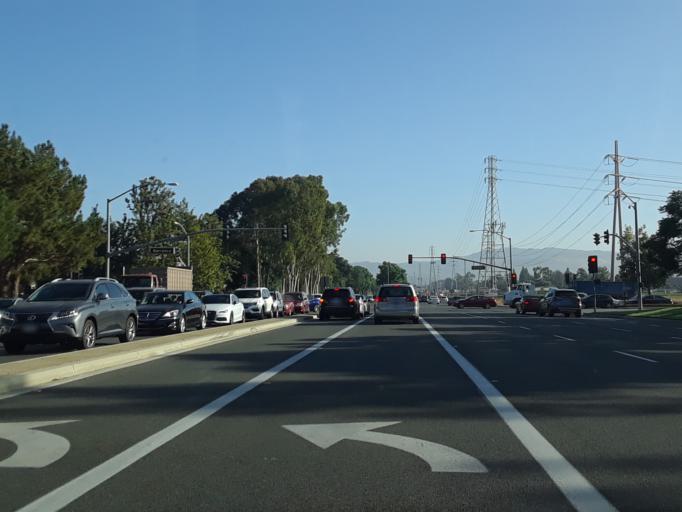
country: US
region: California
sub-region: Orange County
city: Irvine
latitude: 33.6729
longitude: -117.7853
